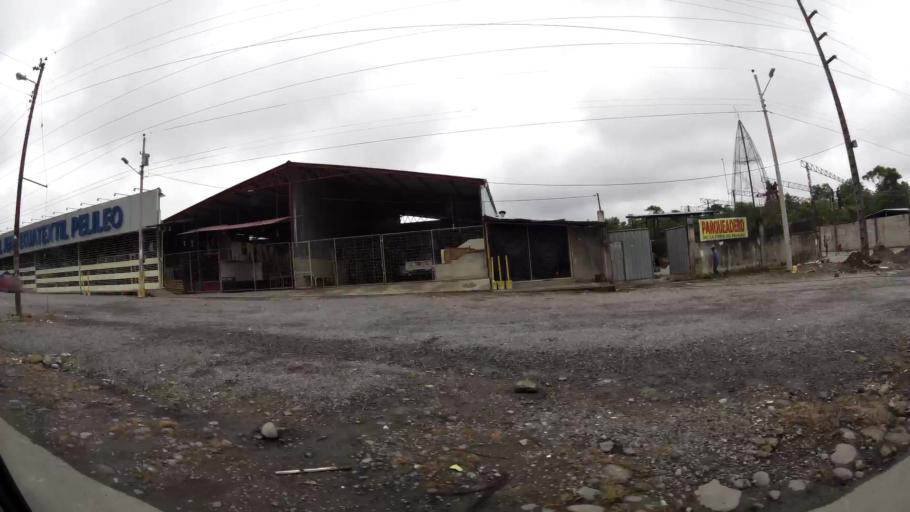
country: EC
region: Santo Domingo de los Tsachilas
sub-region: Canton Santo Domingo de los Colorados
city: Santo Domingo de los Colorados
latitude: -0.2332
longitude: -79.1588
